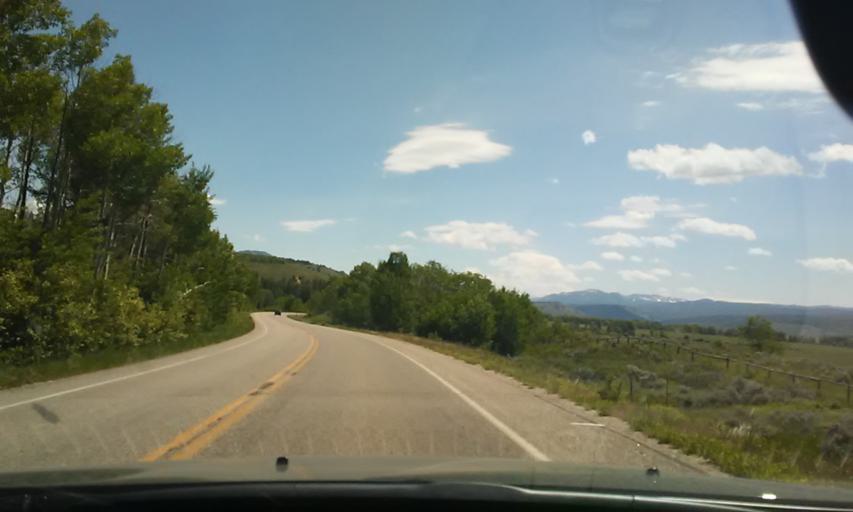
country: US
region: Wyoming
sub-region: Teton County
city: Jackson
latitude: 43.8381
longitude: -110.4804
